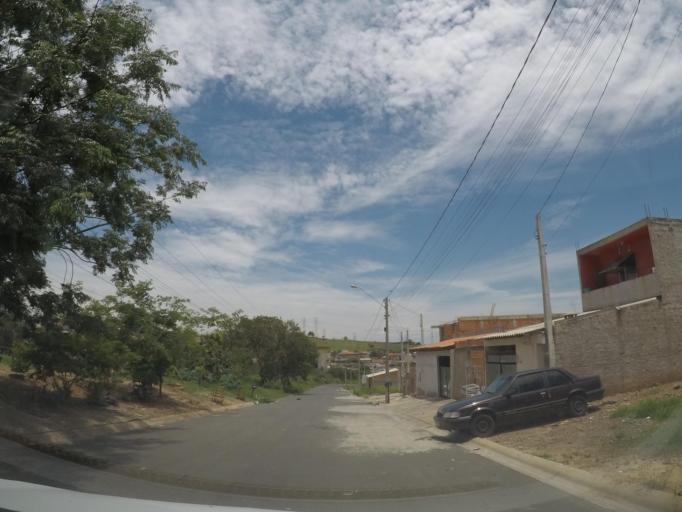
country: BR
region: Sao Paulo
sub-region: Hortolandia
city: Hortolandia
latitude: -22.8436
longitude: -47.2014
